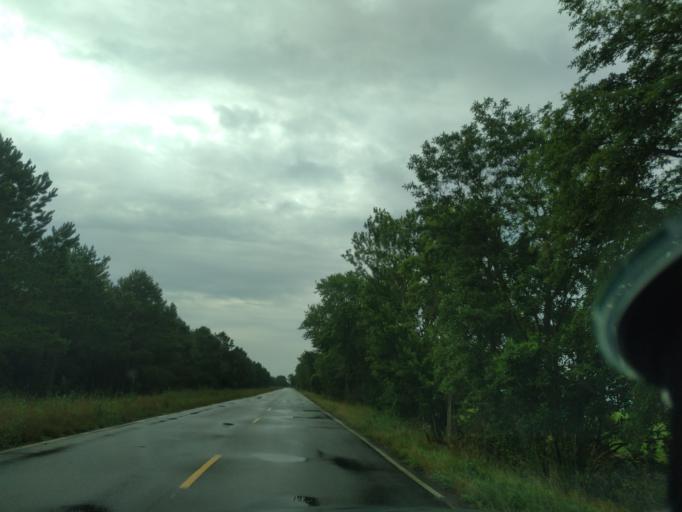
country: US
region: North Carolina
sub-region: Washington County
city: Plymouth
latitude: 35.8469
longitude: -76.5579
